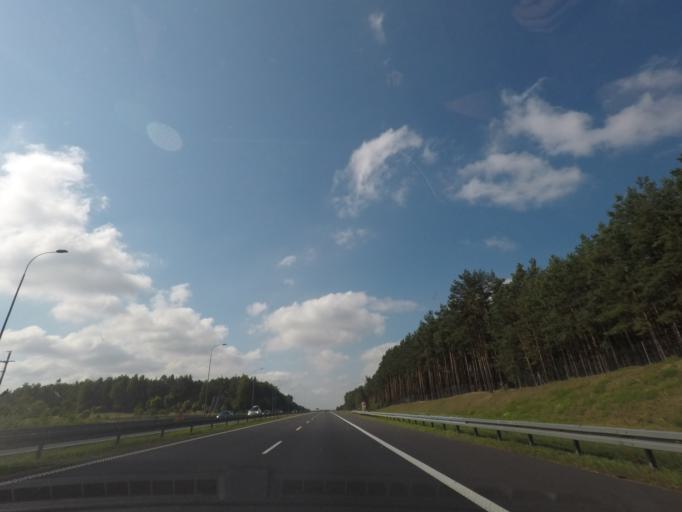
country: PL
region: Kujawsko-Pomorskie
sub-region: Powiat swiecki
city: Warlubie
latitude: 53.6301
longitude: 18.6397
